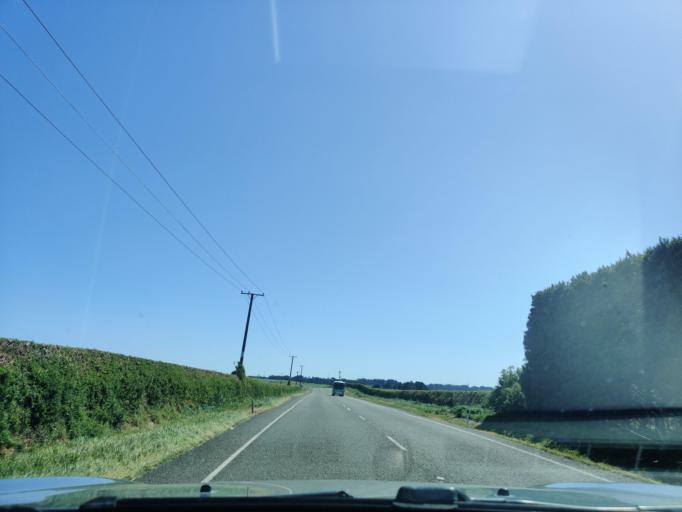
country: NZ
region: Taranaki
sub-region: South Taranaki District
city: Patea
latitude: -39.7861
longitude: 174.6989
